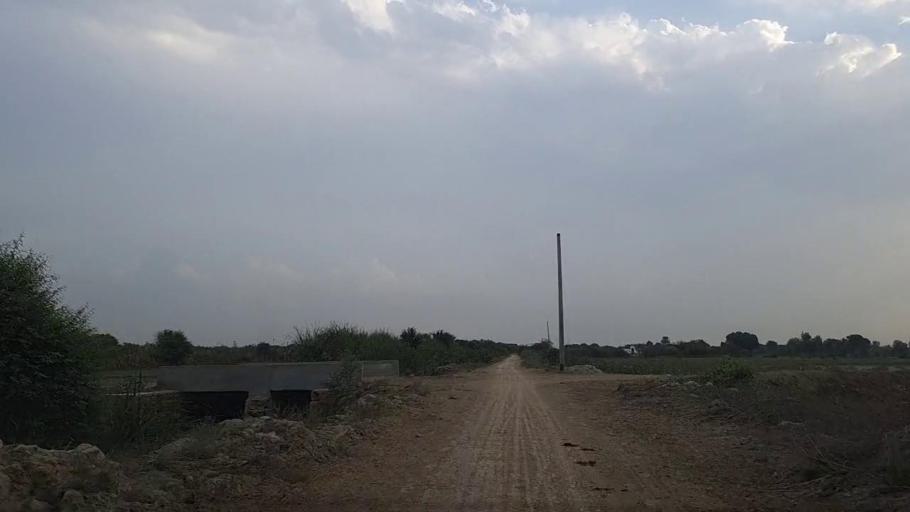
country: PK
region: Sindh
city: Daro Mehar
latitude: 24.7693
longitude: 68.1539
